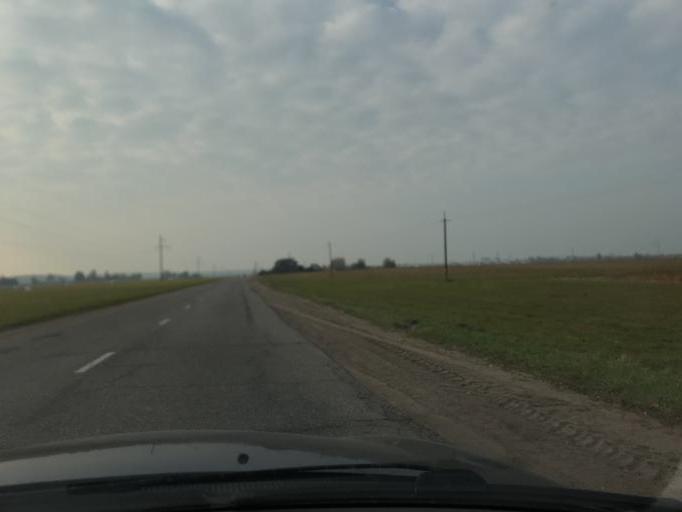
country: BY
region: Grodnenskaya
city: Lida
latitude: 53.8566
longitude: 25.3174
